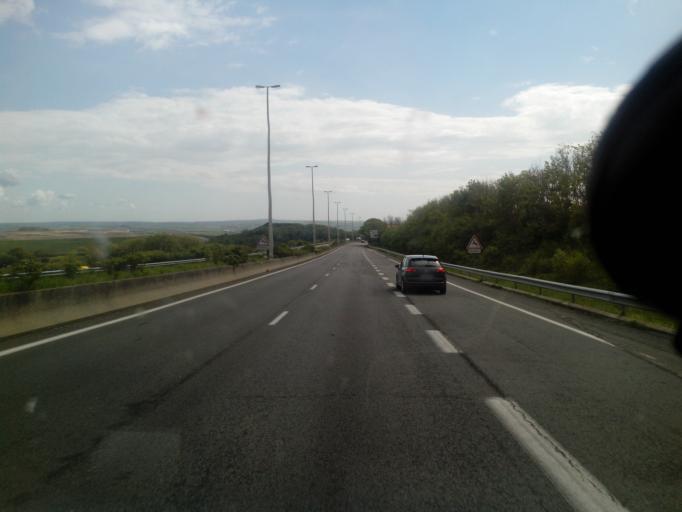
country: FR
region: Nord-Pas-de-Calais
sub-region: Departement du Pas-de-Calais
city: Ferques
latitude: 50.8572
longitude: 1.7312
